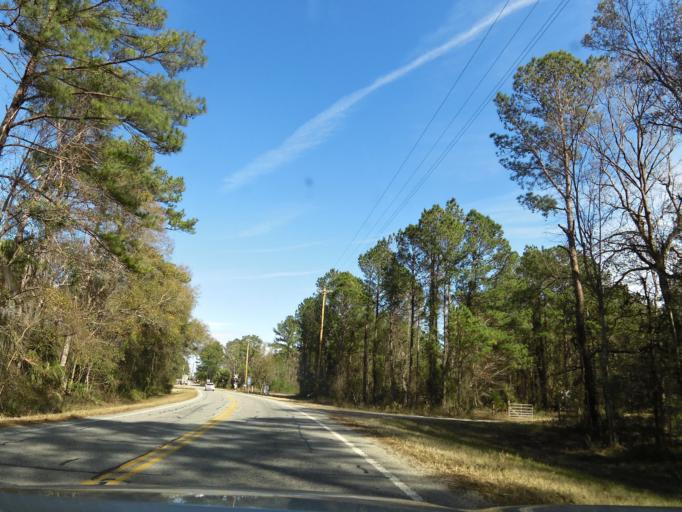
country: US
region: Georgia
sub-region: Glynn County
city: Dock Junction
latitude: 31.2538
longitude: -81.6051
